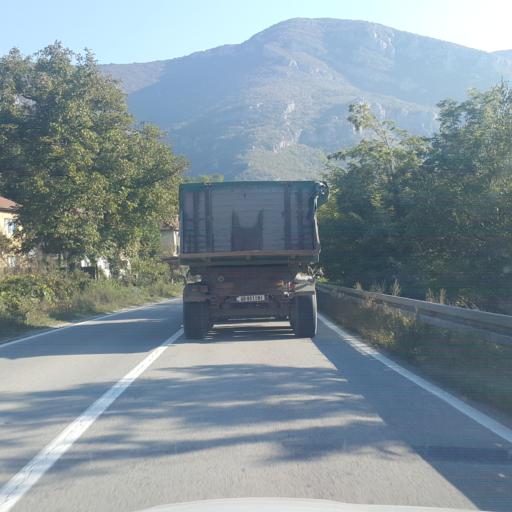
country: RS
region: Central Serbia
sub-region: Nisavski Okrug
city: Svrljig
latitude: 43.3328
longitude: 22.1172
